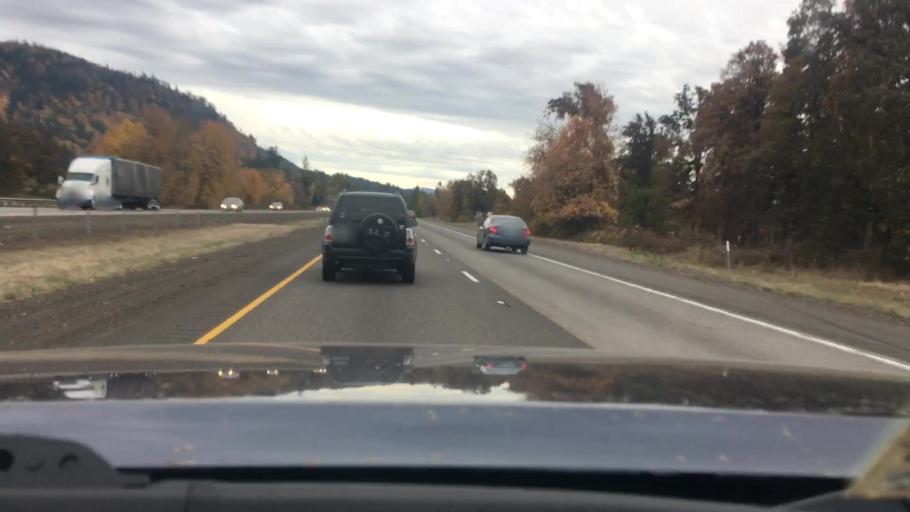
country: US
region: Oregon
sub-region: Lane County
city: Creswell
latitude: 43.8901
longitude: -123.0144
